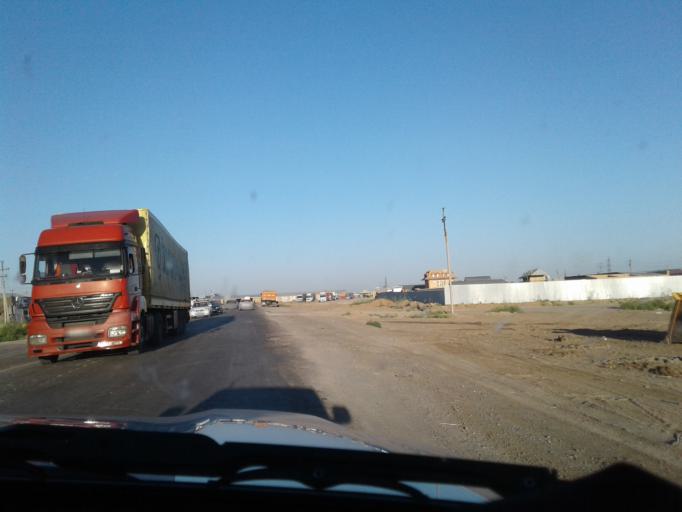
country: TM
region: Mary
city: Mary
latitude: 37.5647
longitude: 61.8193
